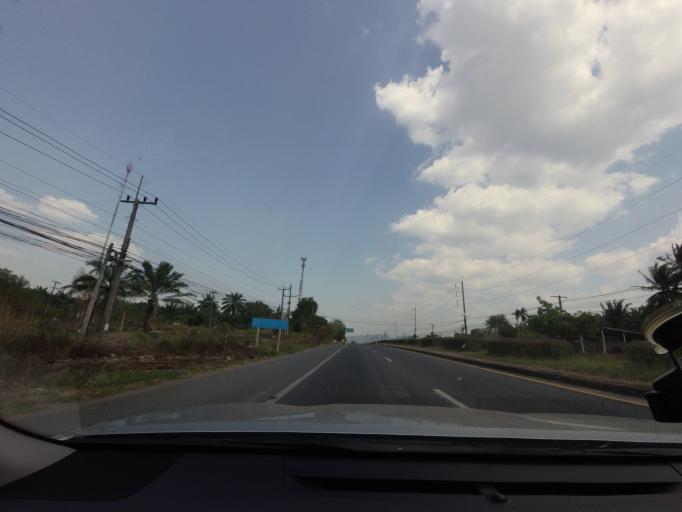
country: TH
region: Phangnga
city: Thap Put
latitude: 8.5073
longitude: 98.6780
